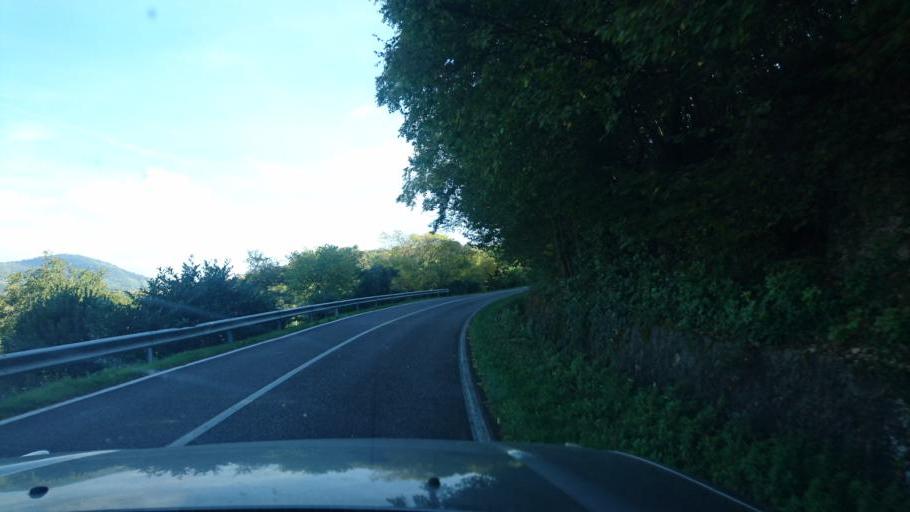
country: IT
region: Veneto
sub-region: Provincia di Padova
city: Baone
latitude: 45.2637
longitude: 11.6961
